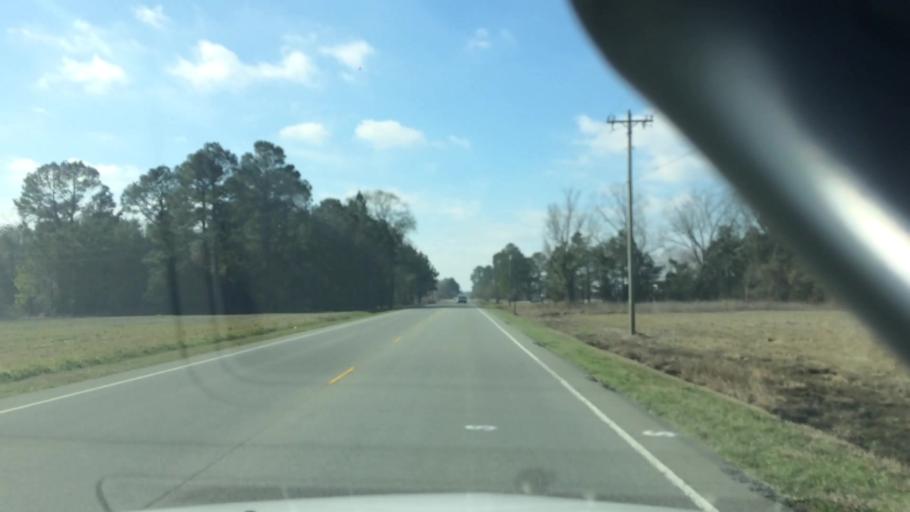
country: US
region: North Carolina
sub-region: Duplin County
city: Wallace
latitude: 34.7909
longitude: -77.8762
